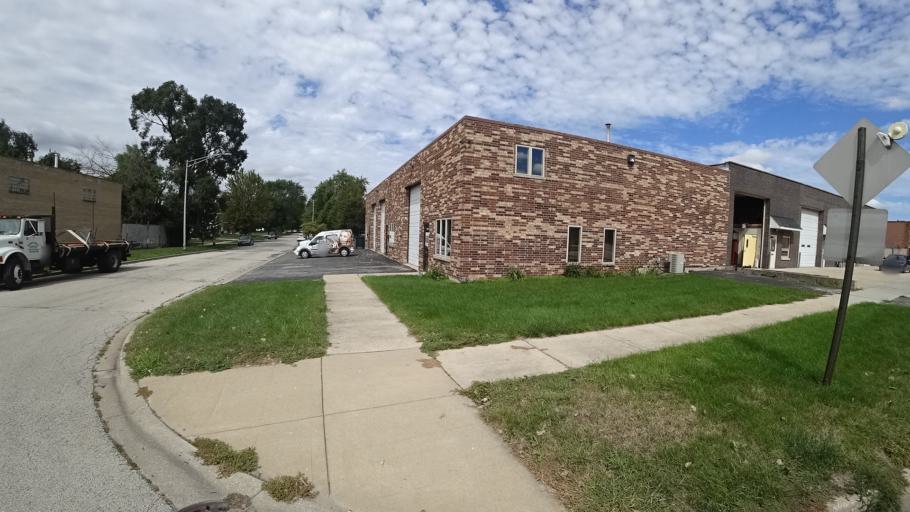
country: US
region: Illinois
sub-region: Cook County
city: Chicago Ridge
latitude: 41.7122
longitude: -87.7881
